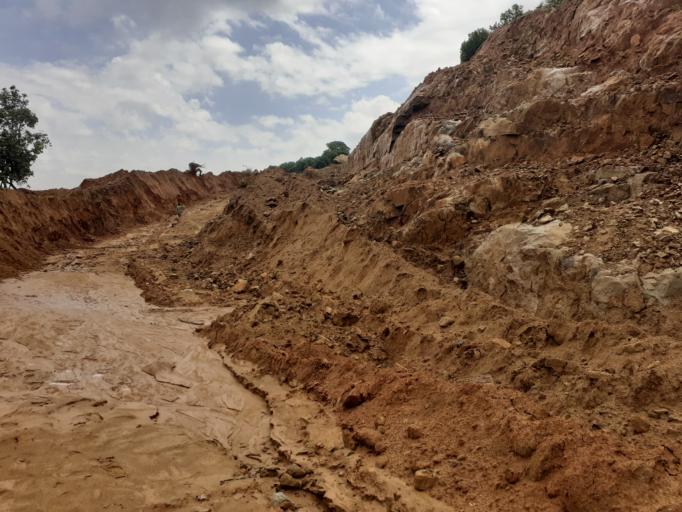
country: ET
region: Oromiya
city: Gimbi
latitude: 9.3267
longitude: 35.6922
